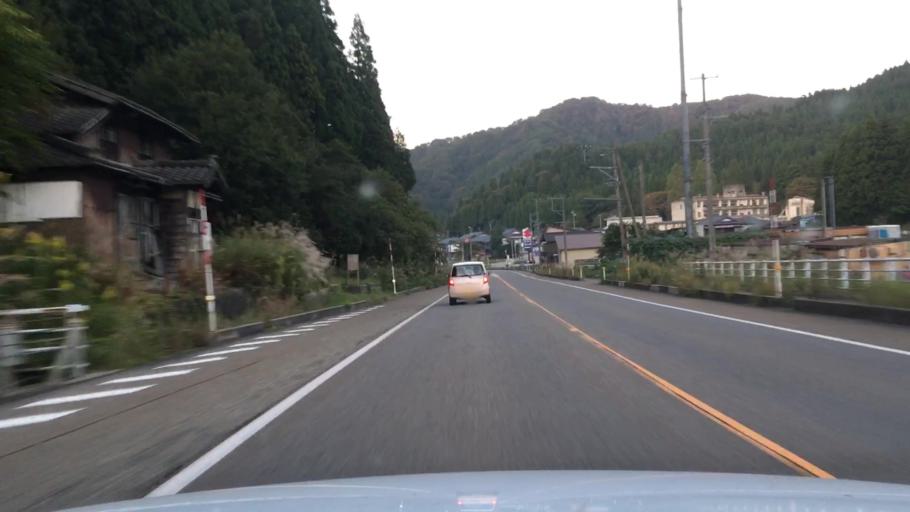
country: JP
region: Niigata
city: Murakami
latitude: 38.4353
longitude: 139.5892
